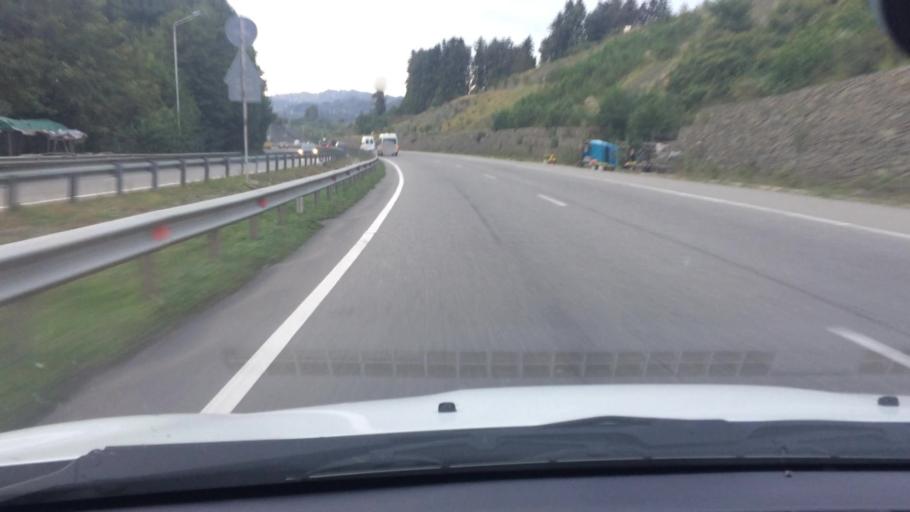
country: GE
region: Ajaria
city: Makhinjauri
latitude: 41.6952
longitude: 41.7266
